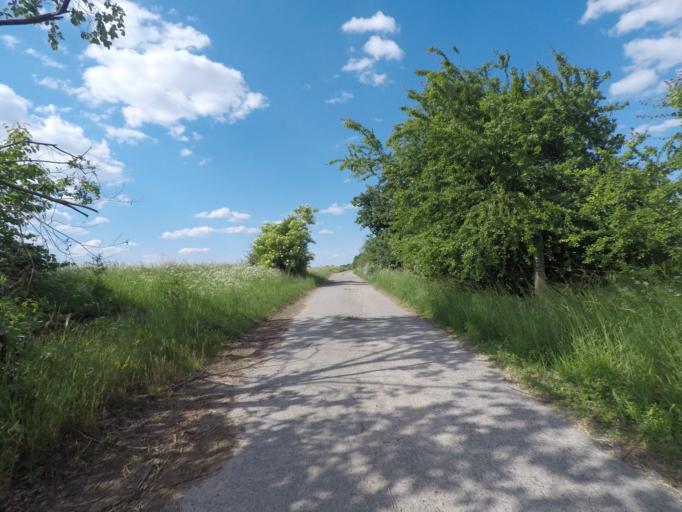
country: DE
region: Brandenburg
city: Britz
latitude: 52.8769
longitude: 13.7282
